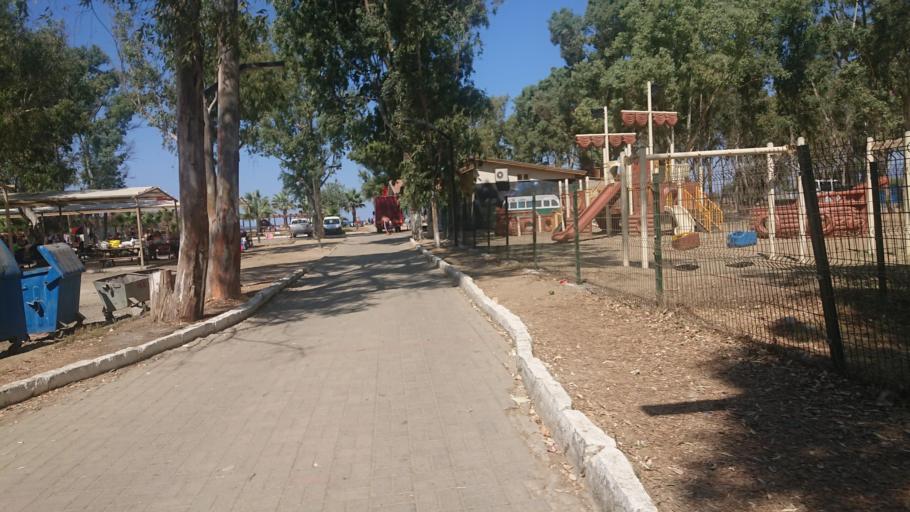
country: TR
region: Aydin
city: Kusadasi
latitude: 37.9371
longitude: 27.2775
